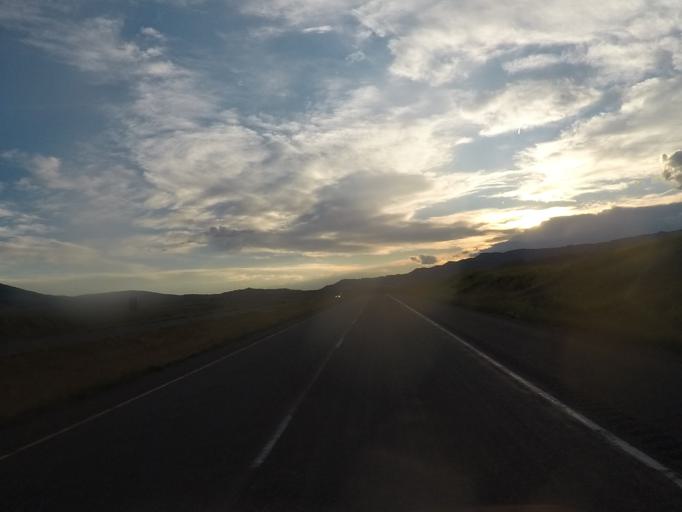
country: US
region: Montana
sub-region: Park County
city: Livingston
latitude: 45.6467
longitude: -110.5936
